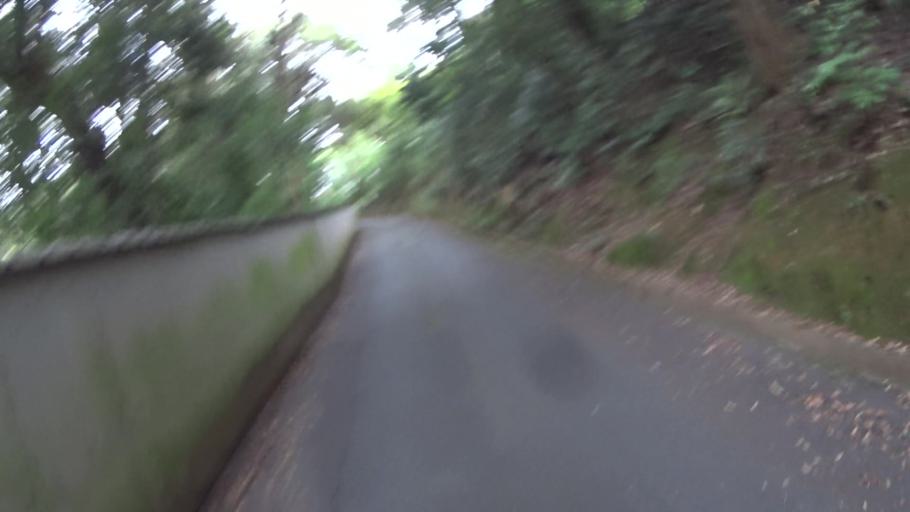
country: JP
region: Kyoto
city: Uji
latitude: 34.9148
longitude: 135.8085
